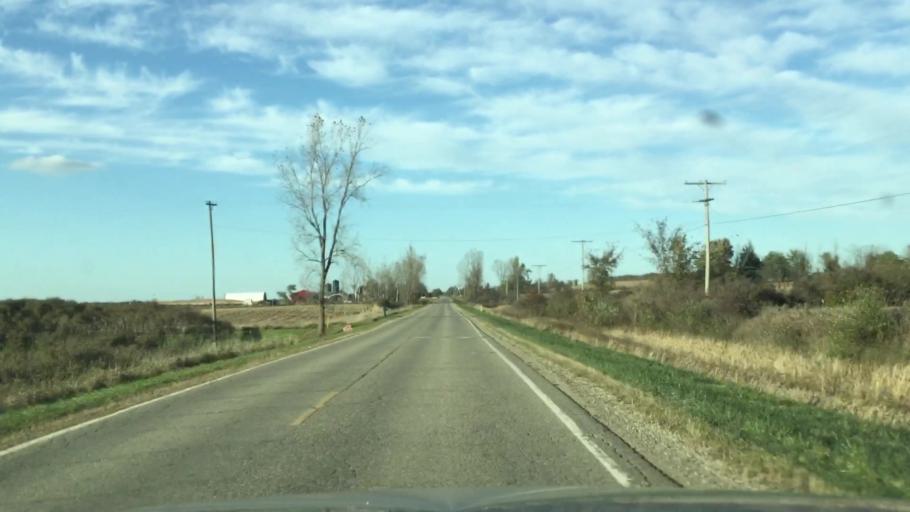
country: US
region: Michigan
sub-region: Lapeer County
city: North Branch
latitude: 43.3048
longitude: -83.1988
